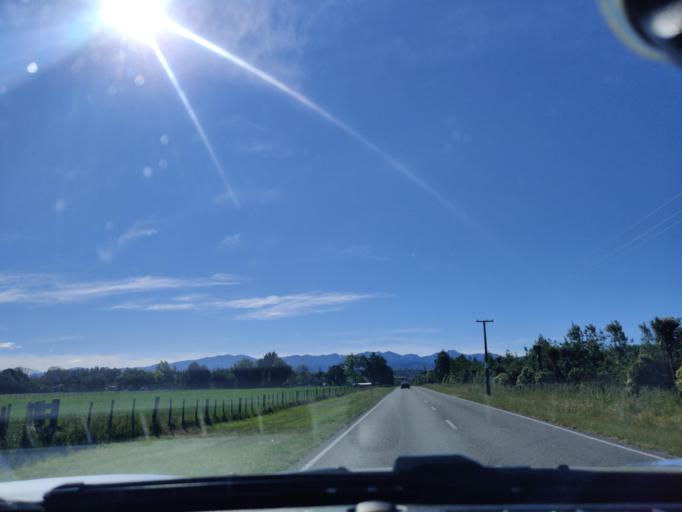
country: NZ
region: Wellington
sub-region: Masterton District
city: Masterton
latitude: -40.9325
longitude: 175.6455
